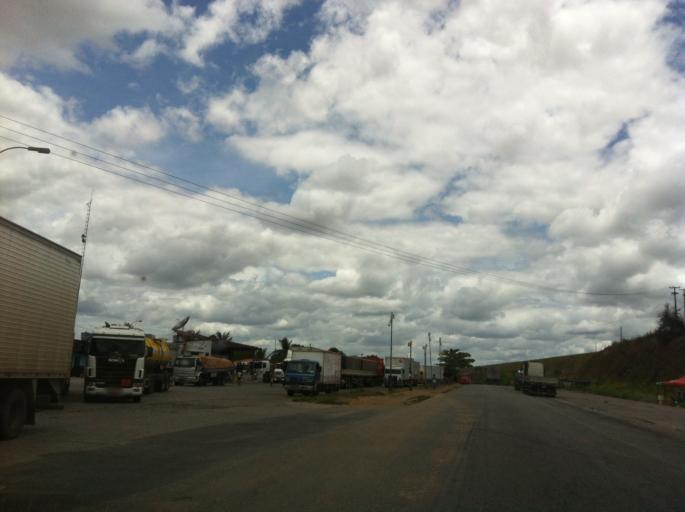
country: BR
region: Alagoas
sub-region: Novo Lino
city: Novo Lino
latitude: -8.8842
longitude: -35.6308
